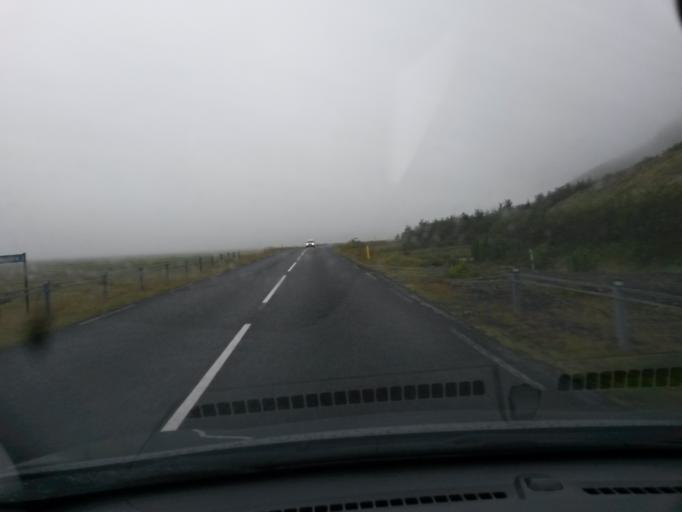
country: IS
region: South
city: Vestmannaeyjar
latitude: 63.4525
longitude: -19.0930
